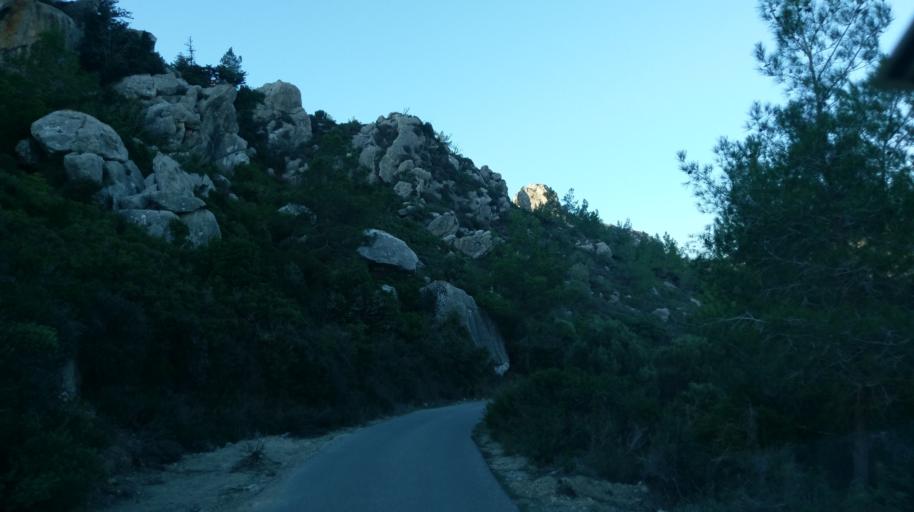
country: CY
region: Ammochostos
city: Trikomo
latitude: 35.3960
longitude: 33.9076
